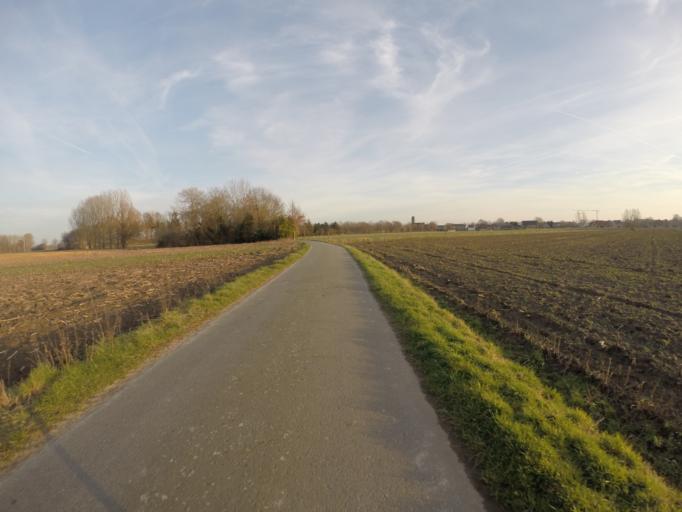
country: BE
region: Flanders
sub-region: Provincie Oost-Vlaanderen
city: Knesselare
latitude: 51.1131
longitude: 3.4270
